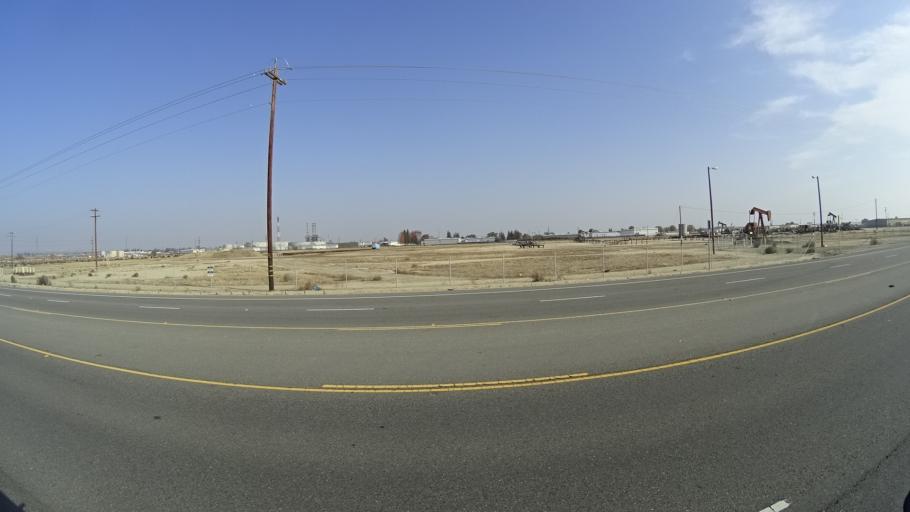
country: US
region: California
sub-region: Kern County
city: Greenacres
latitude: 35.3888
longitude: -119.0657
